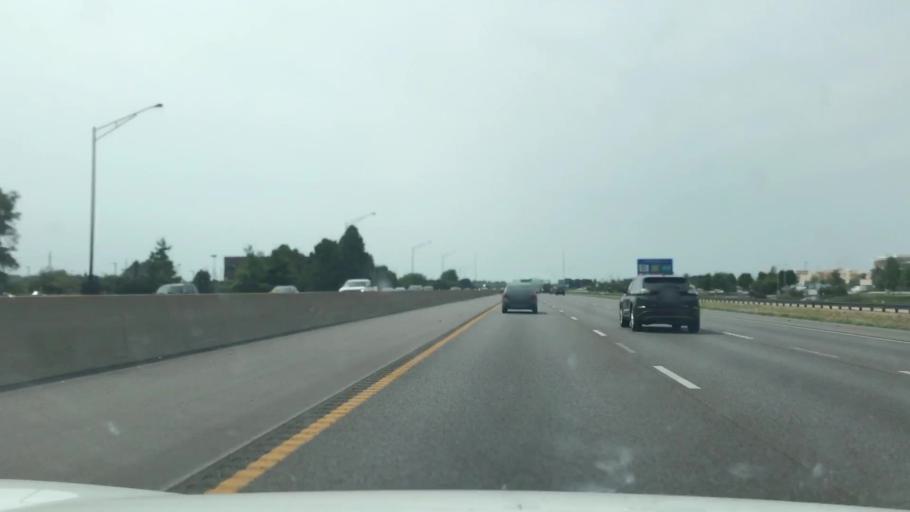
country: US
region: Missouri
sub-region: Saint Louis County
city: Chesterfield
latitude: 38.6692
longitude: -90.5875
